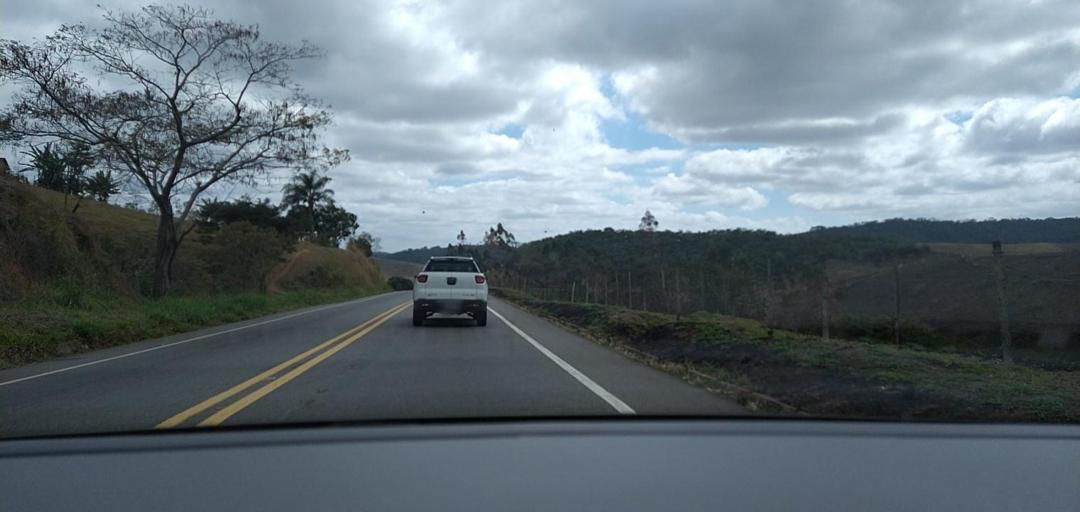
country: BR
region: Minas Gerais
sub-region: Ponte Nova
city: Ponte Nova
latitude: -20.5239
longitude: -42.8943
